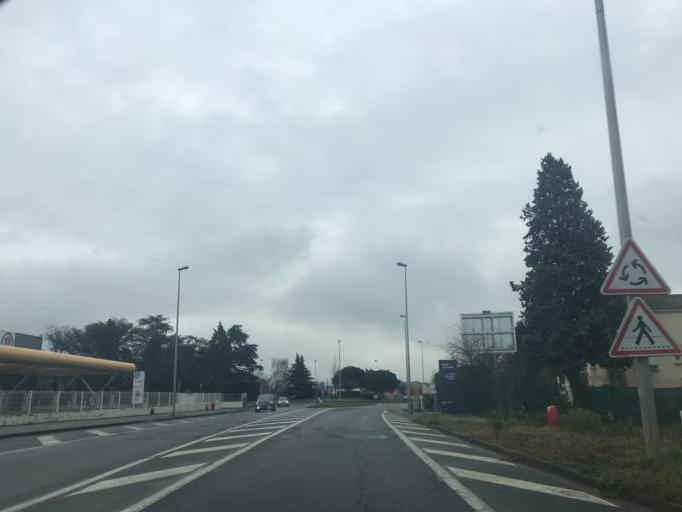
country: FR
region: Rhone-Alpes
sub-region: Departement du Rhone
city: Genay
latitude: 45.8964
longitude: 4.8200
